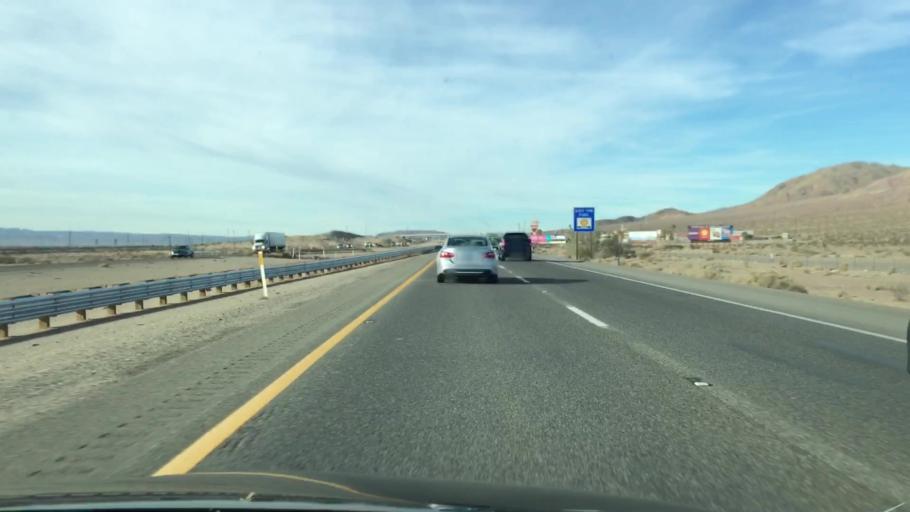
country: US
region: California
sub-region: San Bernardino County
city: Barstow
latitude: 34.9201
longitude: -116.7625
